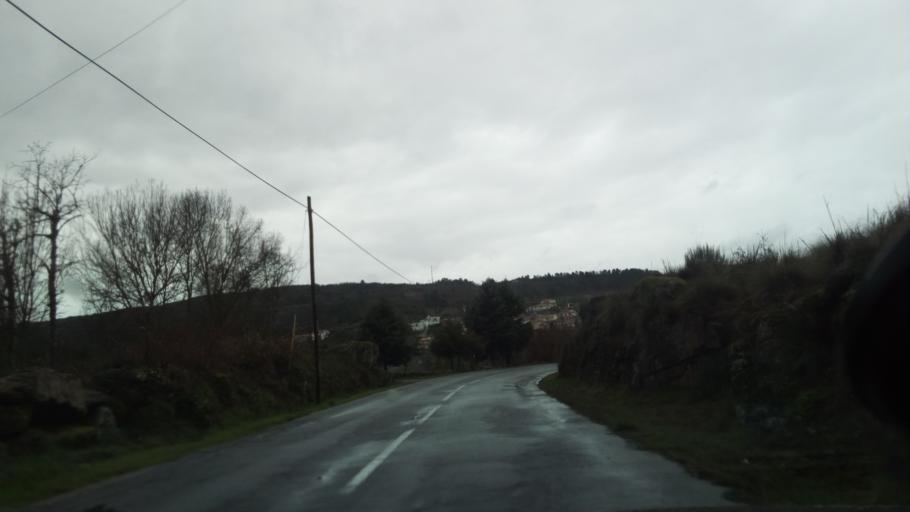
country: PT
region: Guarda
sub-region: Celorico da Beira
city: Celorico da Beira
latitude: 40.6254
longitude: -7.4306
